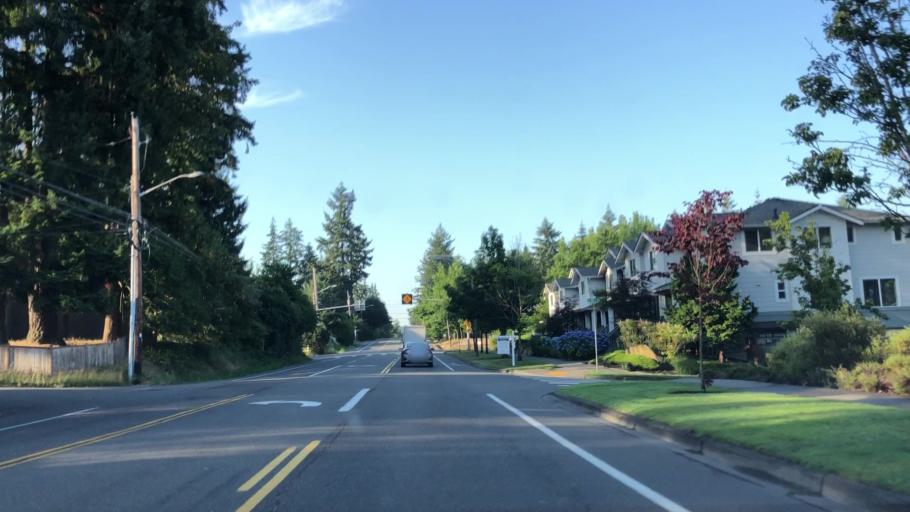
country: US
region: Washington
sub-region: King County
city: Kingsgate
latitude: 47.6987
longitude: -122.1758
